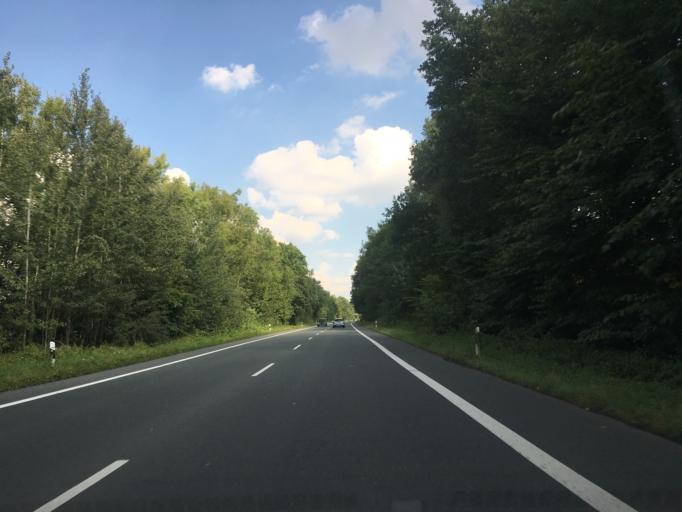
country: DE
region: North Rhine-Westphalia
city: Werne
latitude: 51.6886
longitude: 7.6496
